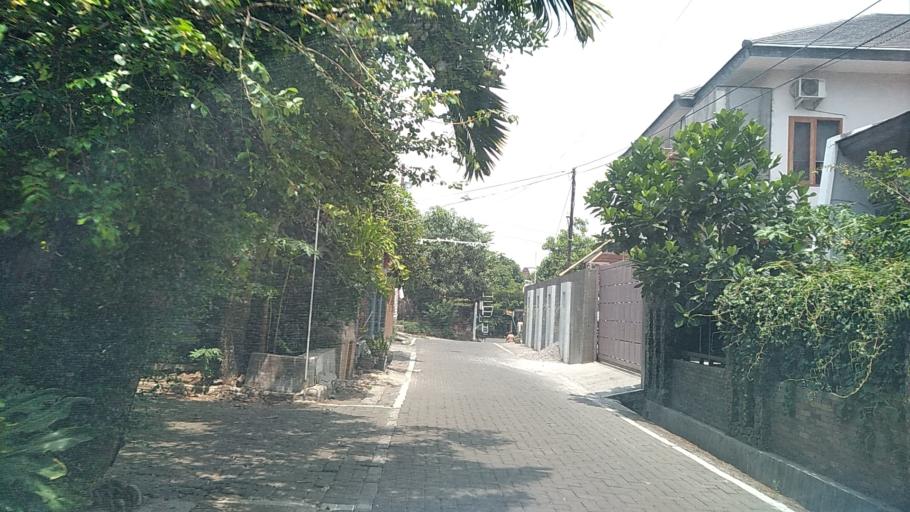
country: ID
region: Central Java
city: Semarang
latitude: -7.0550
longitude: 110.4217
